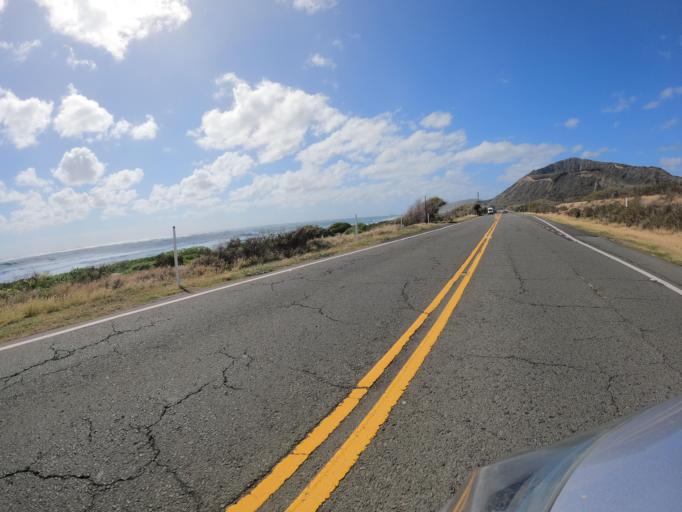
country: US
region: Hawaii
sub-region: Honolulu County
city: Waimanalo Beach
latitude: 21.2930
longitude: -157.6605
